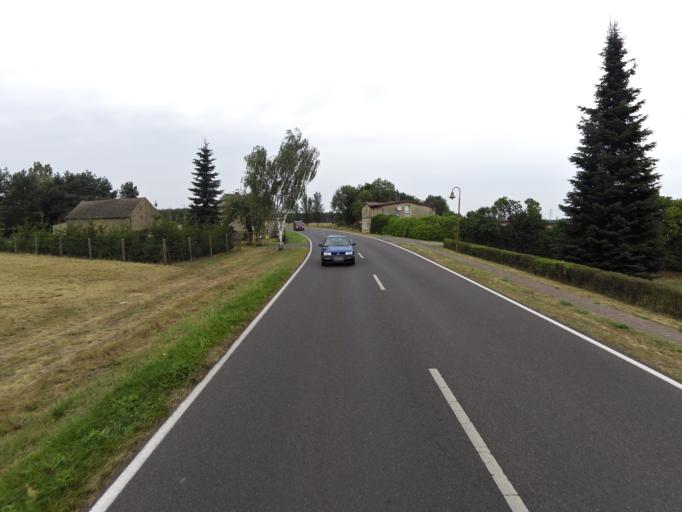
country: DE
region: Brandenburg
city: Zehdenick
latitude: 52.9521
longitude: 13.3814
